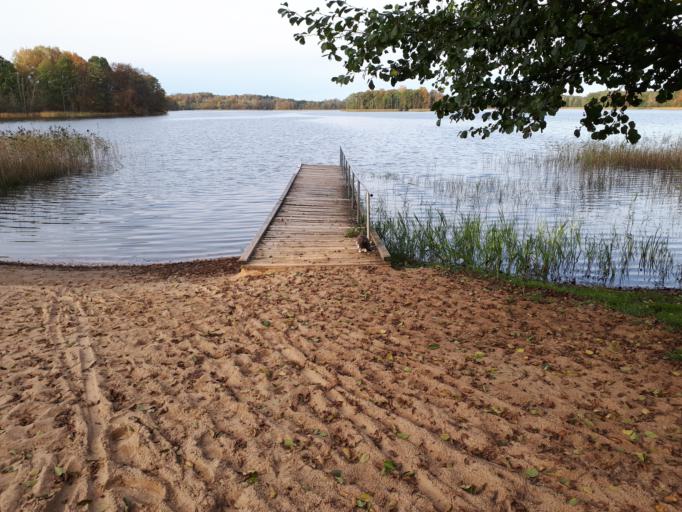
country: LT
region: Utenos apskritis
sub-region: Utena
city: Utena
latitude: 55.4386
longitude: 25.4692
